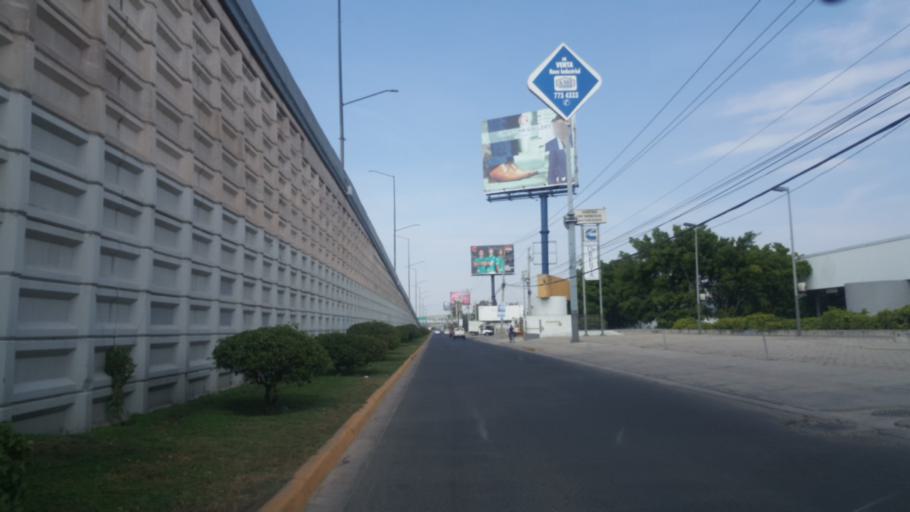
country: MX
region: Guanajuato
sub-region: Leon
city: Fraccionamiento Paraiso Real
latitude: 21.0906
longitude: -101.6208
